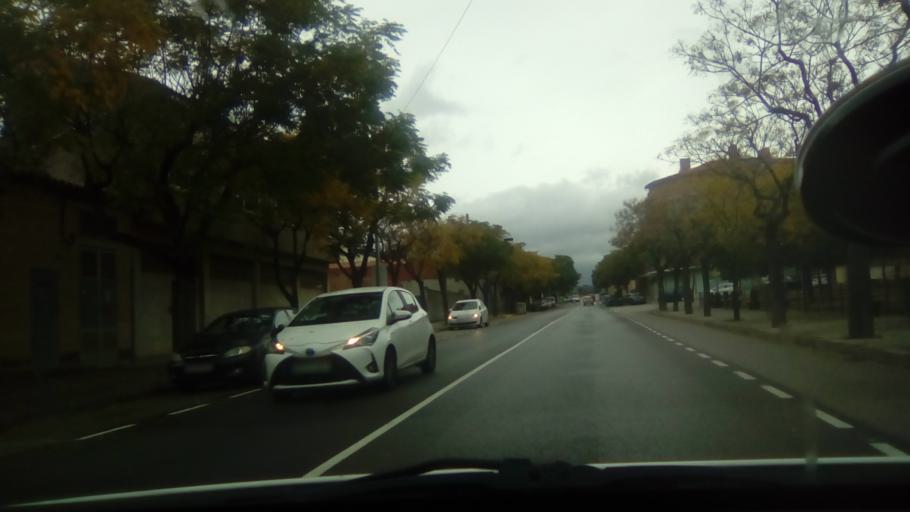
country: ES
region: Catalonia
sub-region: Provincia de Barcelona
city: Monistrol de Montserrat
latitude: 41.6723
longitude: 1.8622
